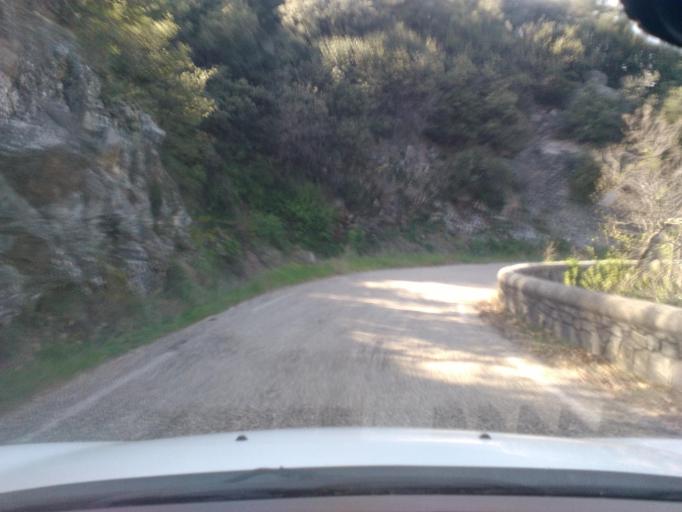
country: FR
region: Languedoc-Roussillon
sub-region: Departement du Gard
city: Lasalle
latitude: 44.0810
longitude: 3.8158
